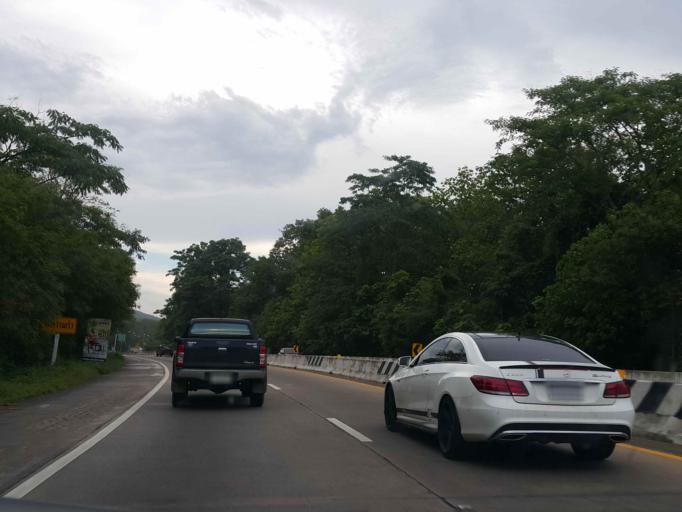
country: TH
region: Lampang
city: Hang Chat
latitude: 18.3493
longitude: 99.2437
